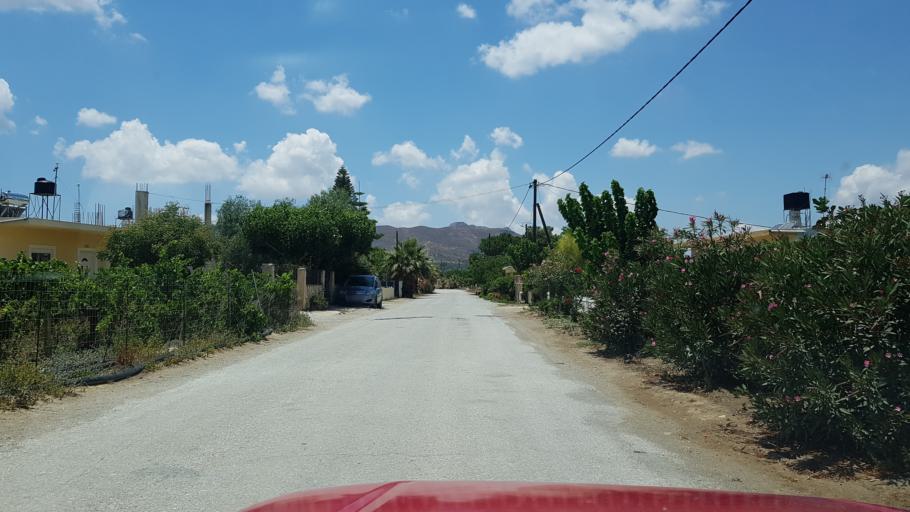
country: GR
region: Crete
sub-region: Nomos Irakleiou
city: Agioi Deka
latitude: 35.0118
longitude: 24.9995
